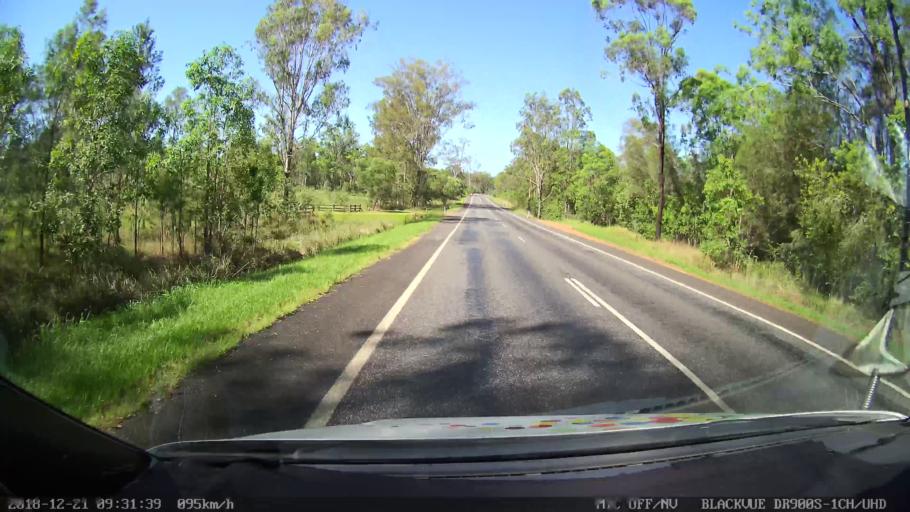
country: AU
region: New South Wales
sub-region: Clarence Valley
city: Maclean
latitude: -29.4622
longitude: 152.9865
